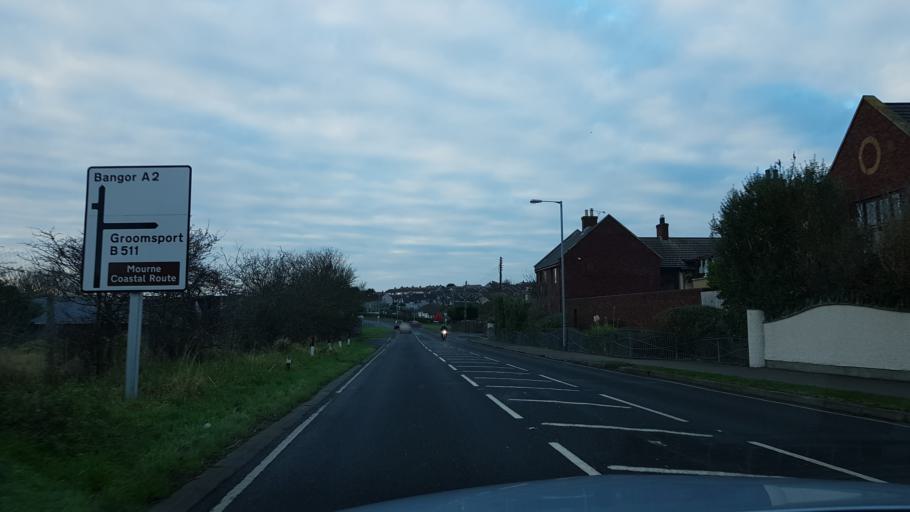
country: GB
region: Northern Ireland
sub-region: North Down District
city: Bangor
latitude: 54.6730
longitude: -5.6114
